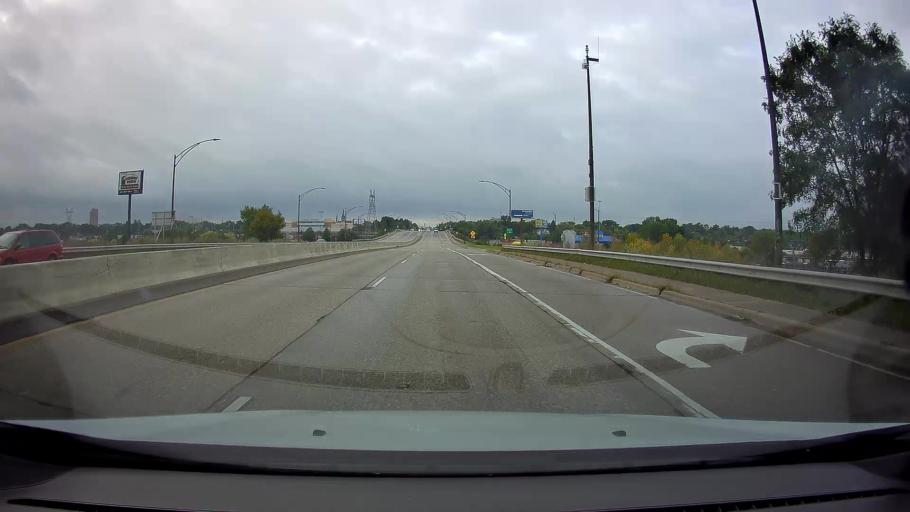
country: US
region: Minnesota
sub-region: Ramsey County
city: Falcon Heights
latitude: 44.9735
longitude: -93.1672
